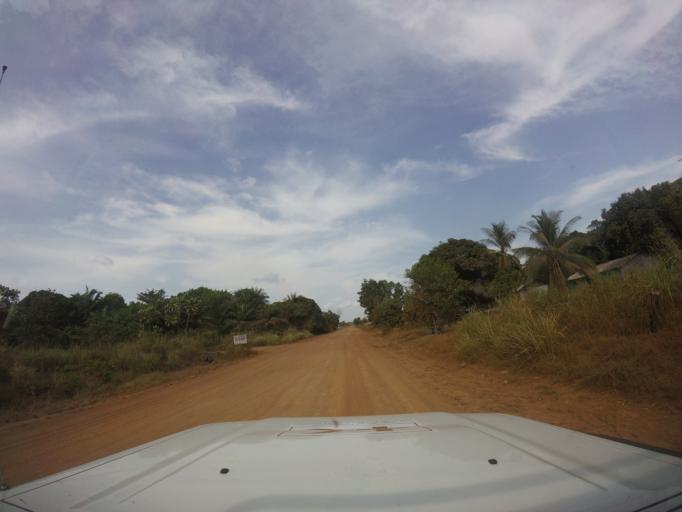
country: LR
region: Grand Cape Mount
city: Robertsport
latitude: 6.6943
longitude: -11.1058
